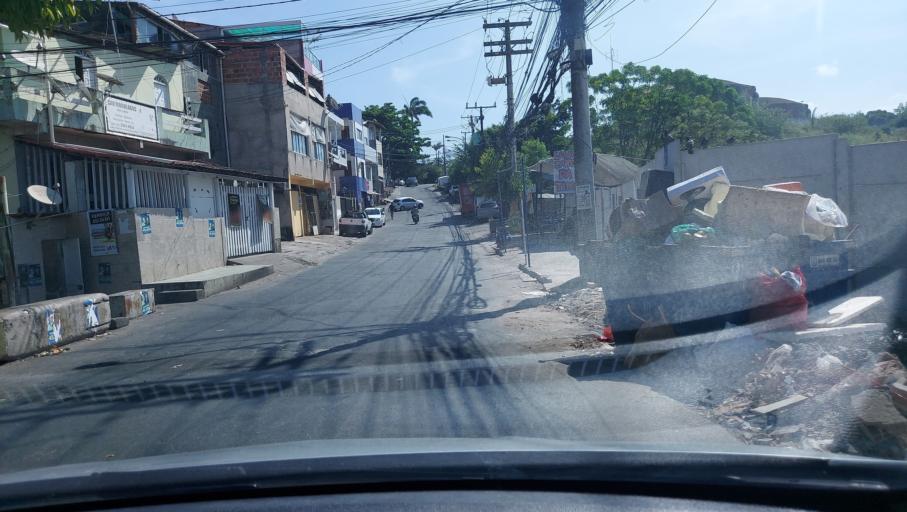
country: BR
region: Bahia
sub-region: Salvador
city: Salvador
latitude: -12.9762
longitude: -38.4373
